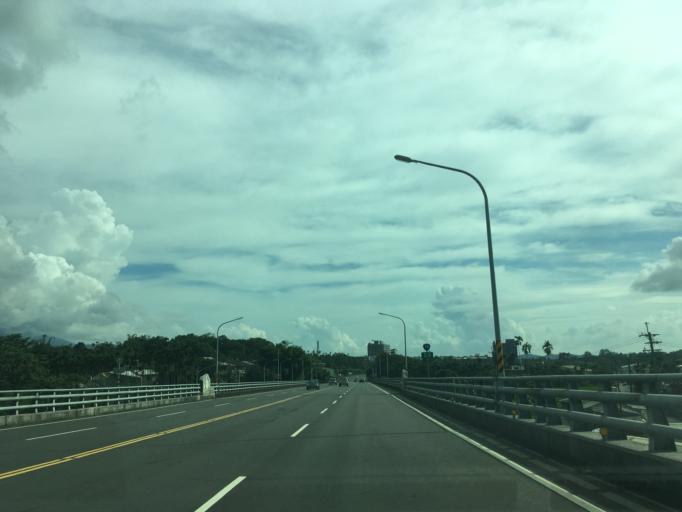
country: TW
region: Taiwan
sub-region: Chiayi
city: Jiayi Shi
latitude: 23.4508
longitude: 120.5503
